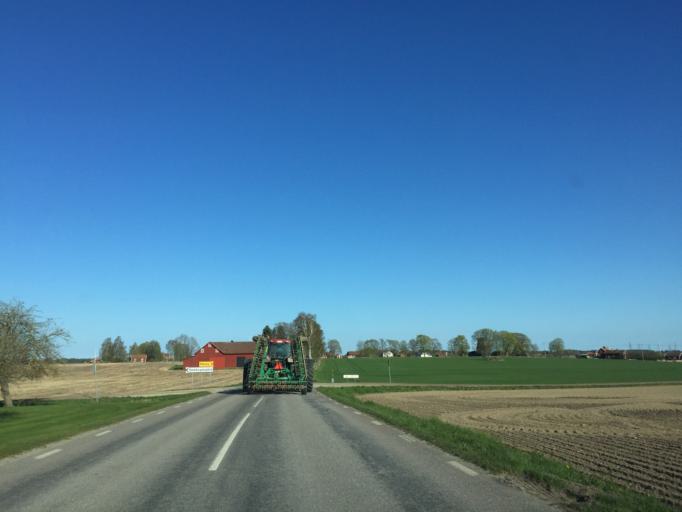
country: SE
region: OErebro
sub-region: Orebro Kommun
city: Odensbacken
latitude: 59.2048
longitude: 15.5416
